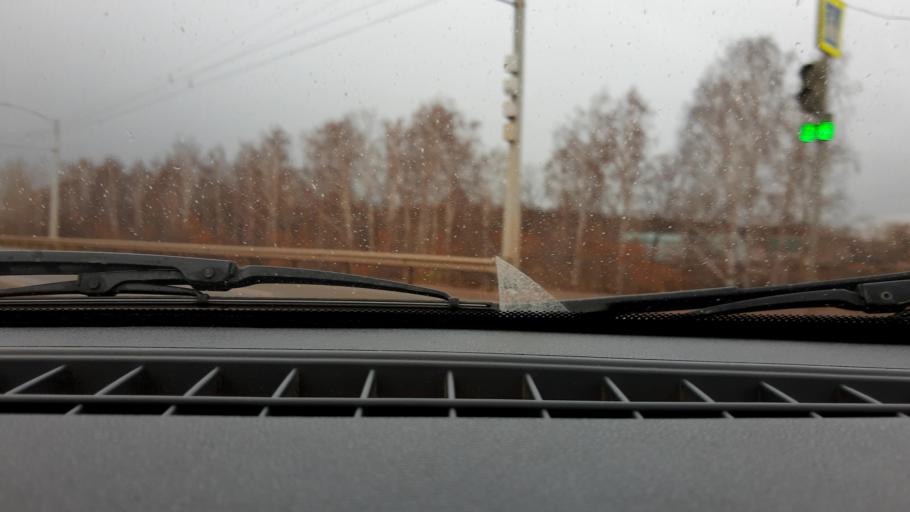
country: RU
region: Bashkortostan
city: Mikhaylovka
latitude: 54.7698
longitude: 55.9115
